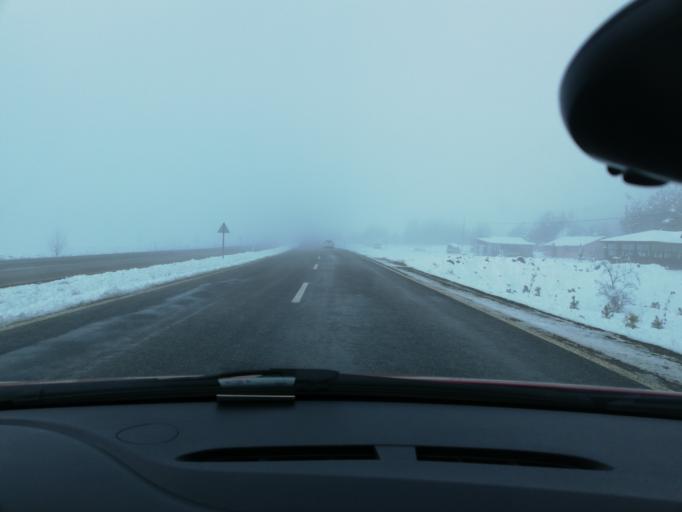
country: TR
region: Kastamonu
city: Akkaya
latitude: 41.2988
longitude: 33.5216
